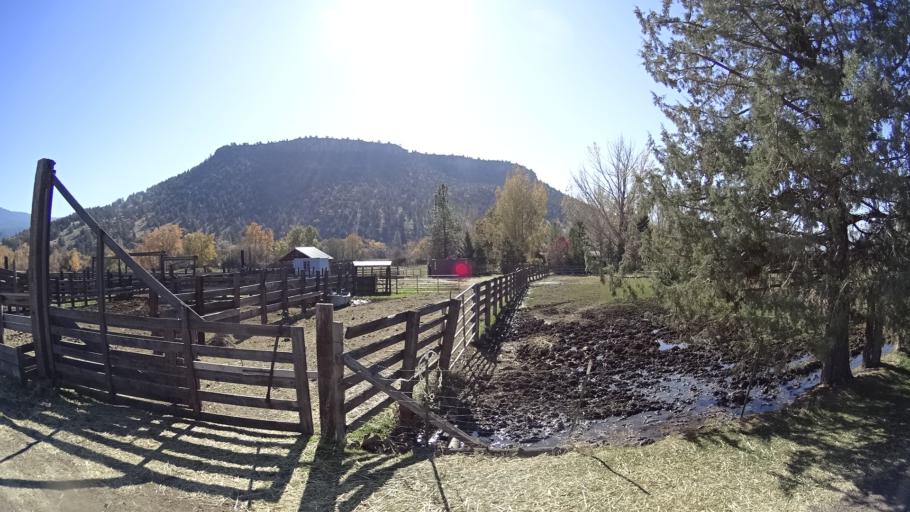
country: US
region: California
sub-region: Siskiyou County
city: Montague
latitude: 41.7398
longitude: -122.3382
